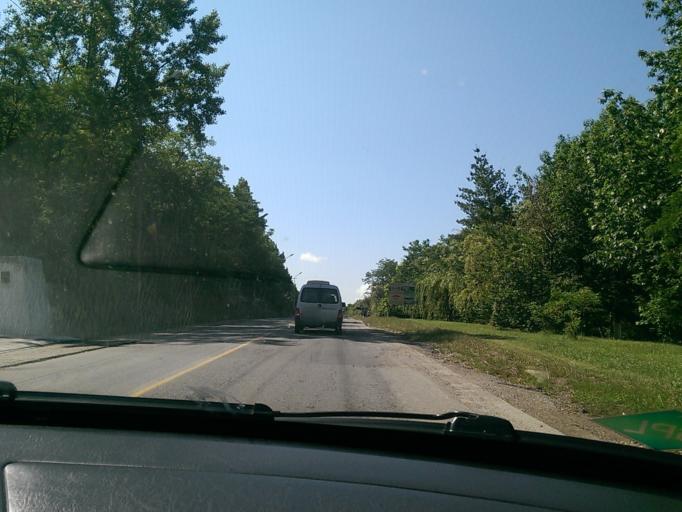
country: RO
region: Bihor
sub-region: Comuna Sanmartin
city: Sanmartin
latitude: 46.9935
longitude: 21.9831
